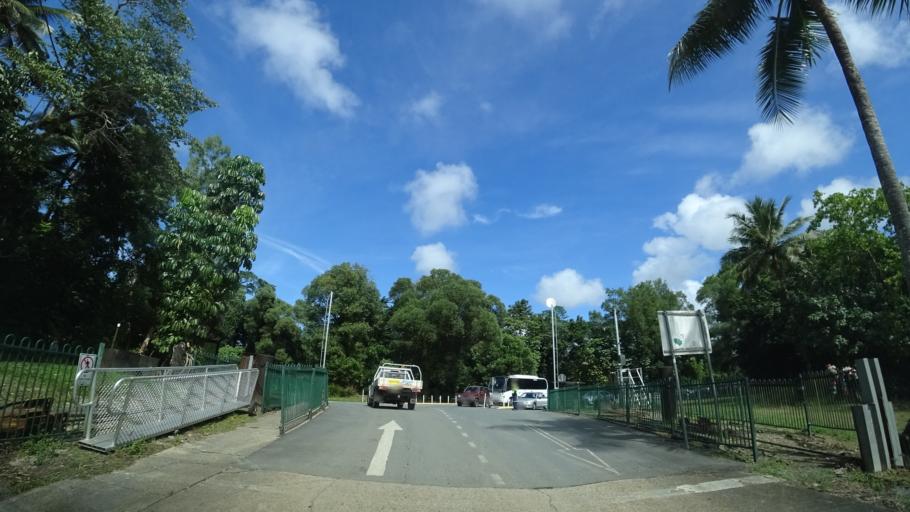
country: AU
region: Queensland
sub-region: Cairns
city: Port Douglas
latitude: -16.2593
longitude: 145.3983
